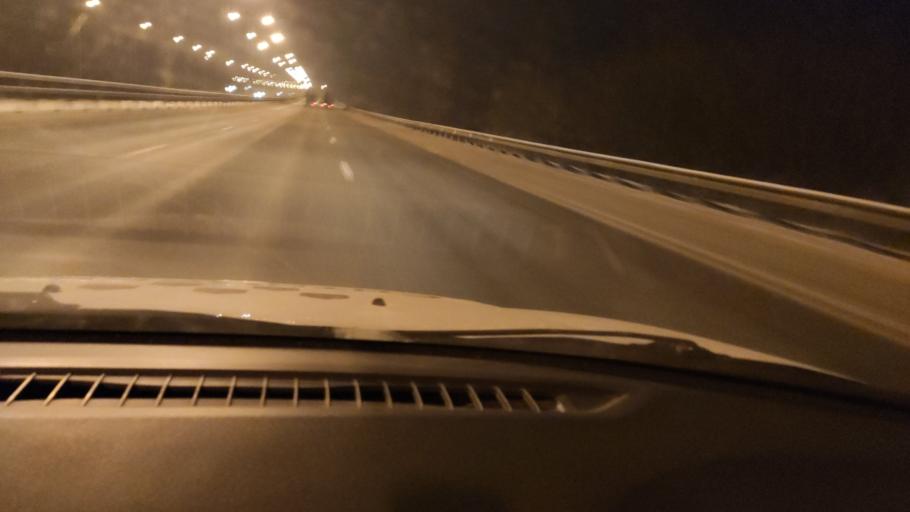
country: RU
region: Perm
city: Kukushtan
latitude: 57.6684
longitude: 56.4366
